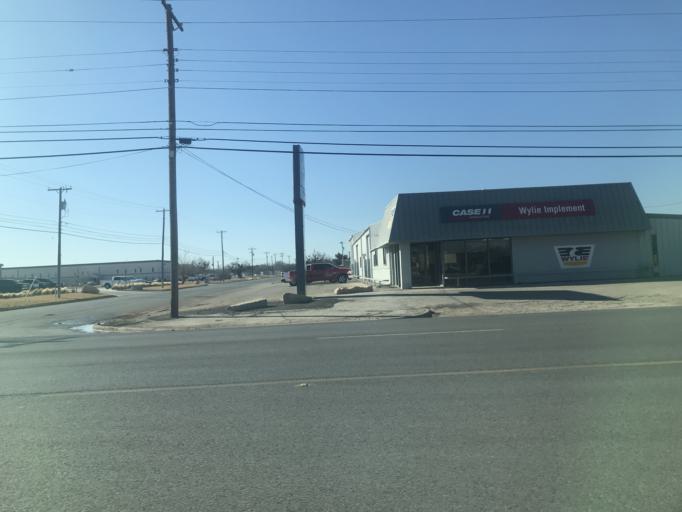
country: US
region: Texas
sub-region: Taylor County
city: Abilene
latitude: 32.4086
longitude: -99.7424
